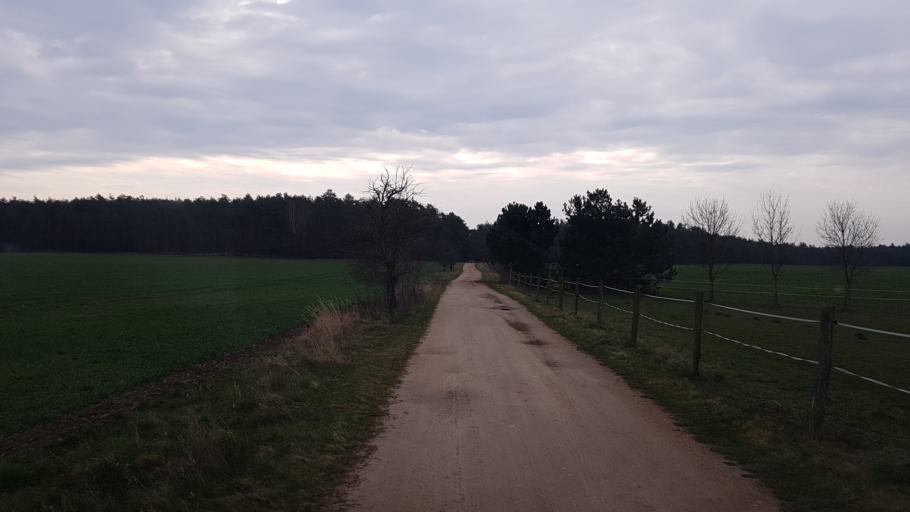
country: DE
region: Brandenburg
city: Schilda
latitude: 51.6309
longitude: 13.3773
